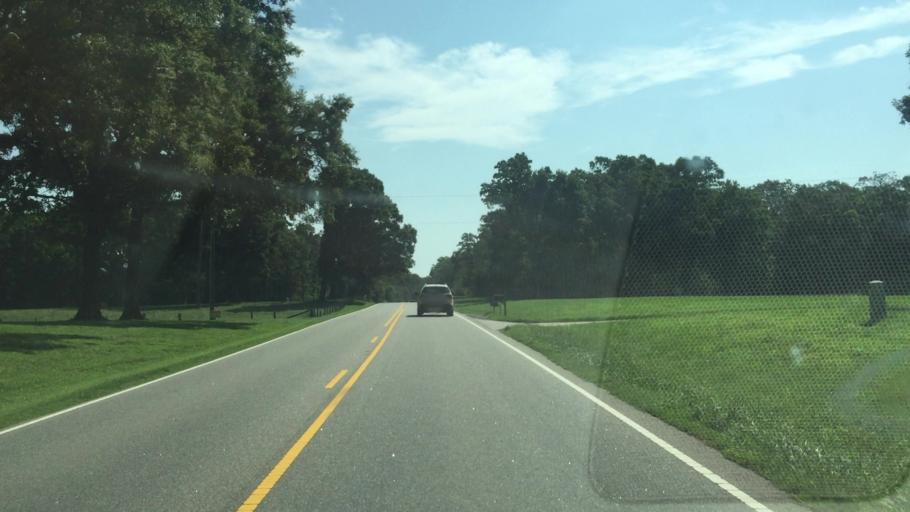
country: US
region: North Carolina
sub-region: Stanly County
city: Stanfield
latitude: 35.1324
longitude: -80.3872
